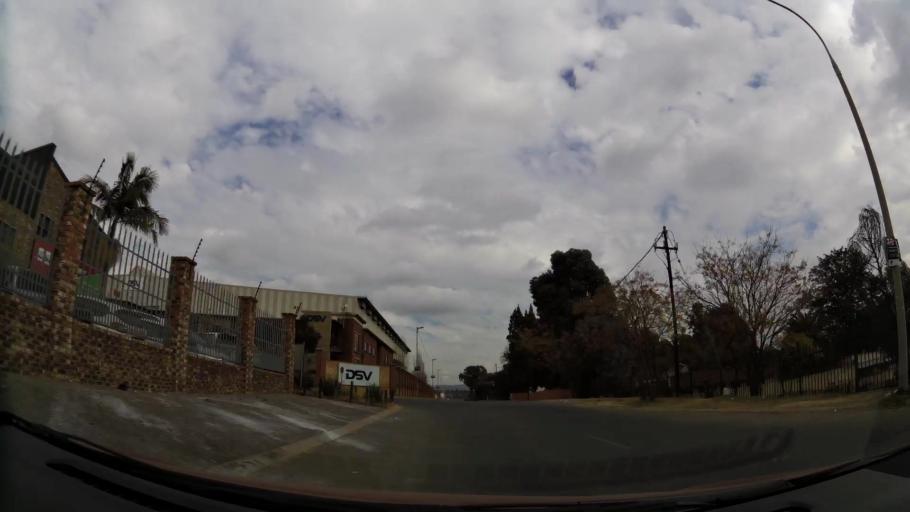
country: ZA
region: Gauteng
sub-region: West Rand District Municipality
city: Muldersdriseloop
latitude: -26.0793
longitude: 27.9104
